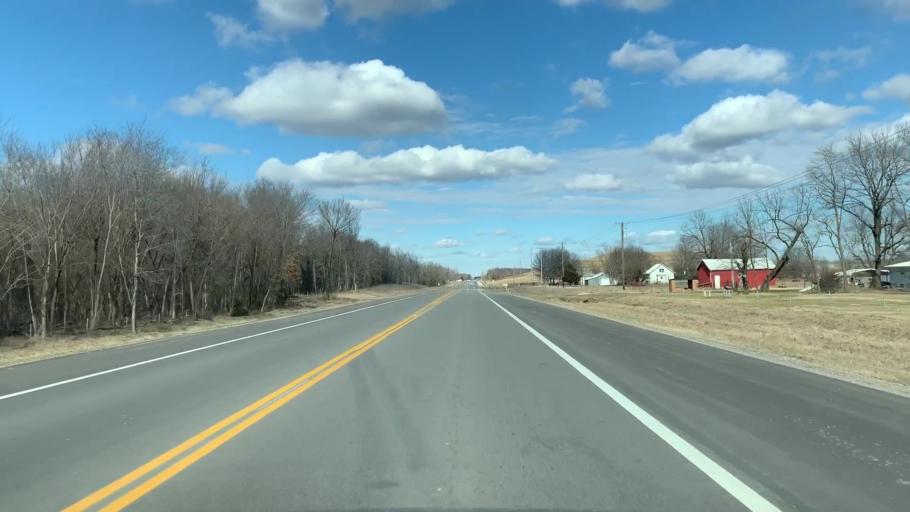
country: US
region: Kansas
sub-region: Cherokee County
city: Columbus
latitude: 37.2323
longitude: -94.8319
